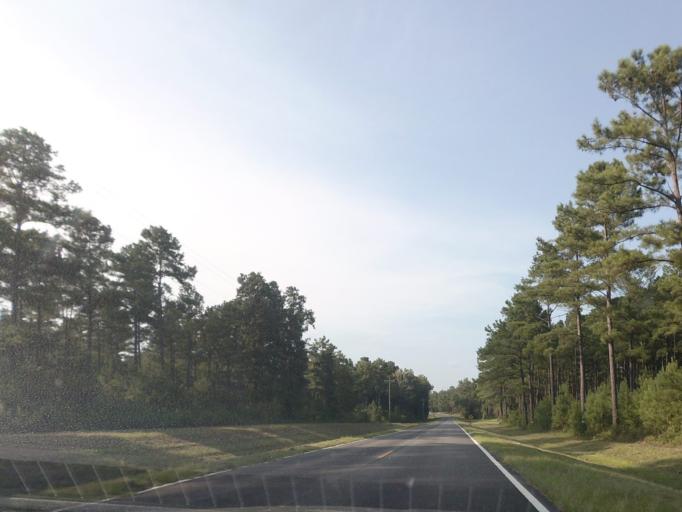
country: US
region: Georgia
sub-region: Bleckley County
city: Cochran
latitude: 32.4557
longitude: -83.2987
